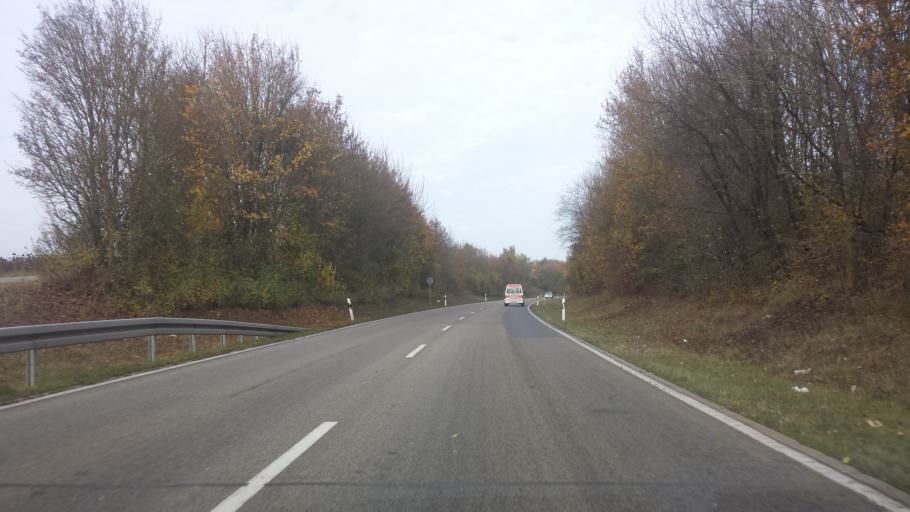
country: DE
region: Baden-Wuerttemberg
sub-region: Regierungsbezirk Stuttgart
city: Bad Rappenau
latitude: 49.2199
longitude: 9.0800
